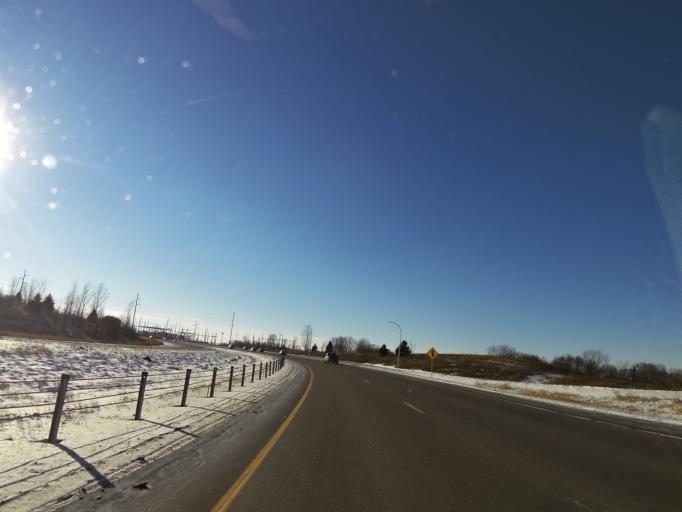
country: US
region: Minnesota
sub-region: Scott County
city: Shakopee
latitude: 44.7779
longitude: -93.5623
